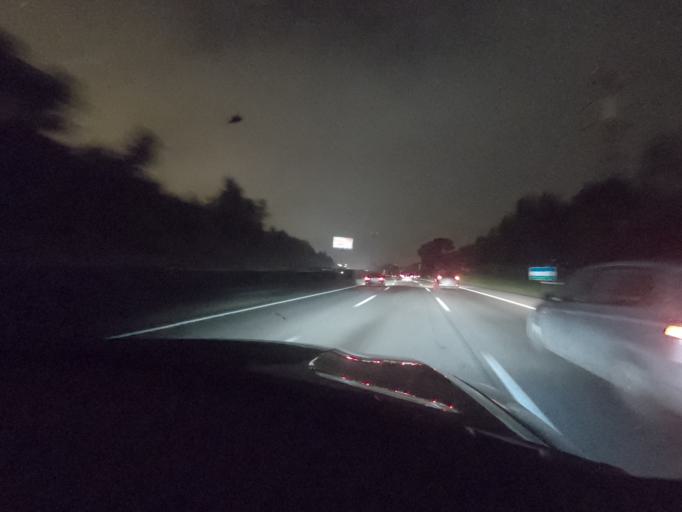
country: PT
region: Lisbon
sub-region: Vila Franca de Xira
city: Vialonga
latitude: 38.8655
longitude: -9.0787
